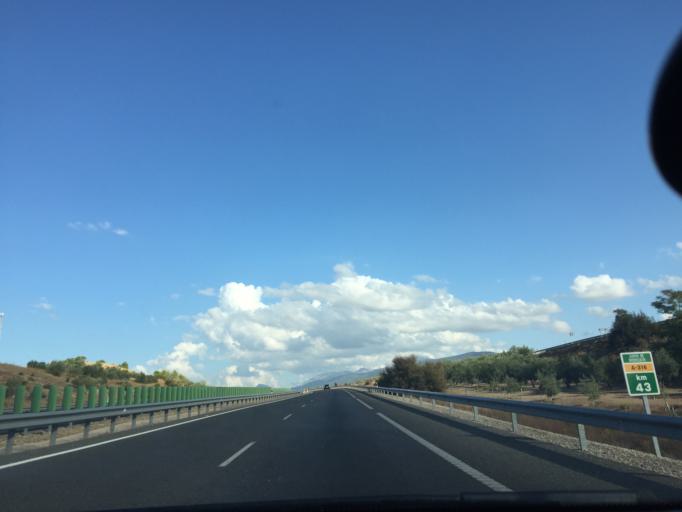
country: ES
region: Andalusia
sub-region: Provincia de Jaen
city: La Guardia de Jaen
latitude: 37.8017
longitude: -3.7013
